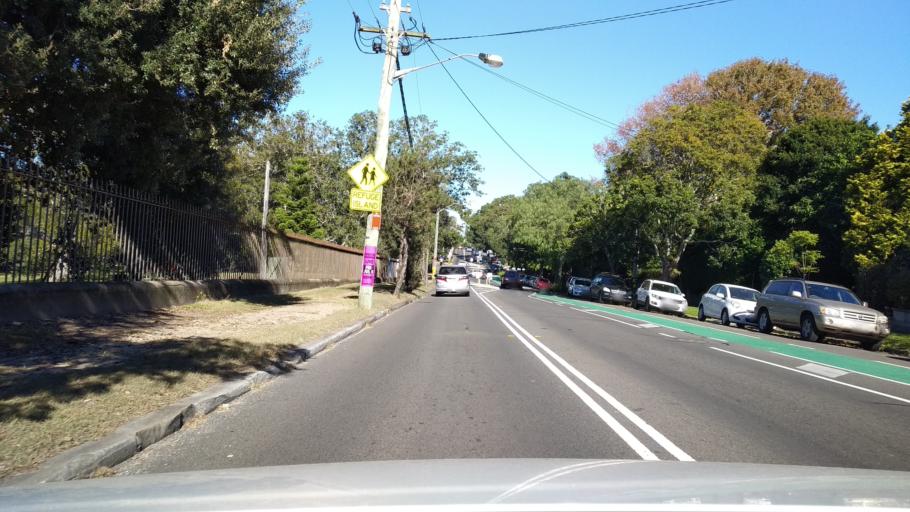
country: AU
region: New South Wales
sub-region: Woollahra
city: Woollahra
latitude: -33.8936
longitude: 151.2314
